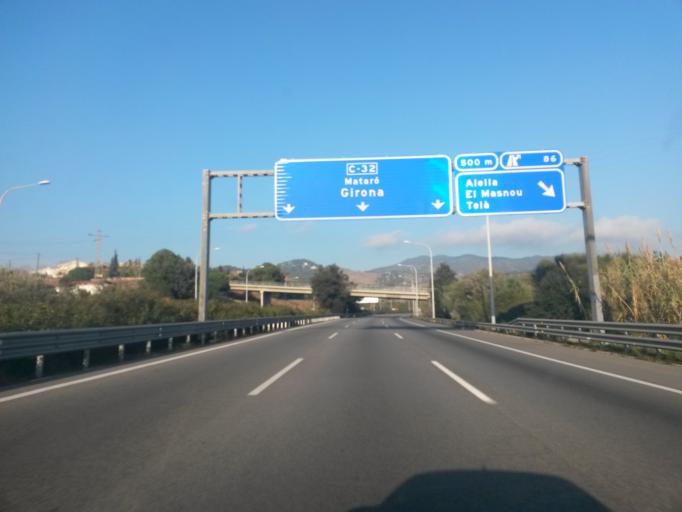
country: ES
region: Catalonia
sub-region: Provincia de Barcelona
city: Alella
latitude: 41.4850
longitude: 2.2961
